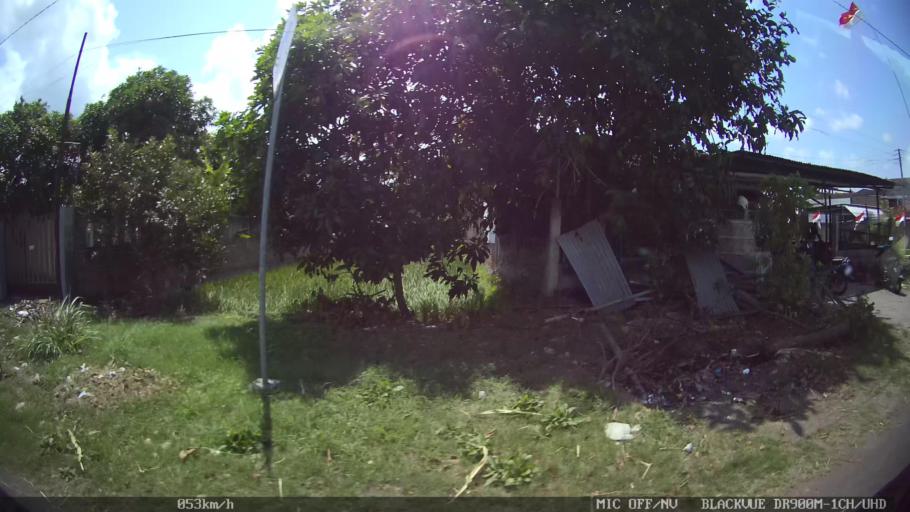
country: ID
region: Daerah Istimewa Yogyakarta
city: Sewon
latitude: -7.8828
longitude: 110.3457
